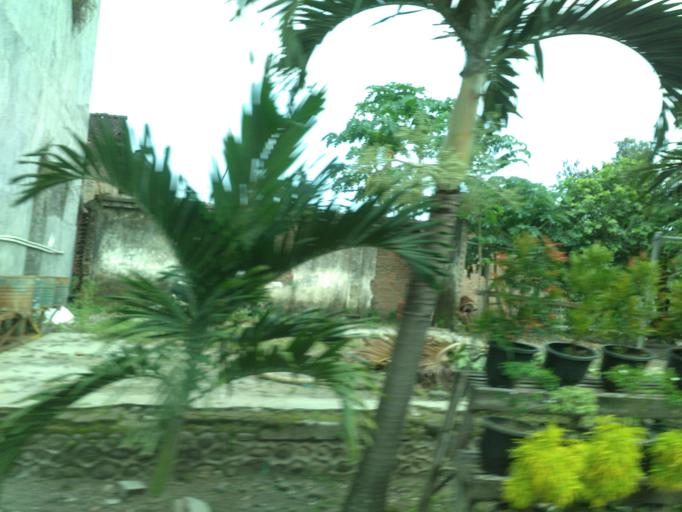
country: ID
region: Central Java
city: Klaten
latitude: -7.6868
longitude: 110.6313
